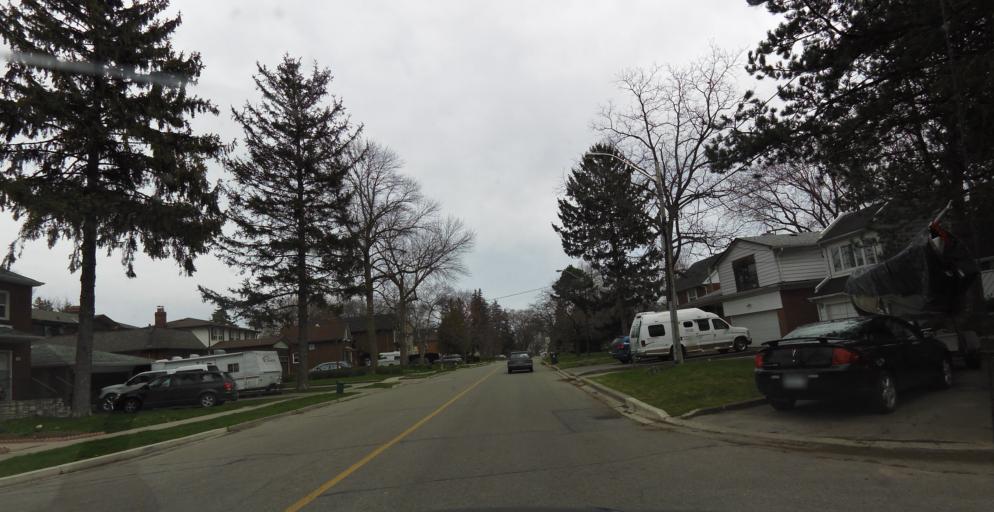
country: CA
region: Ontario
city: Etobicoke
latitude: 43.5905
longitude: -79.5253
